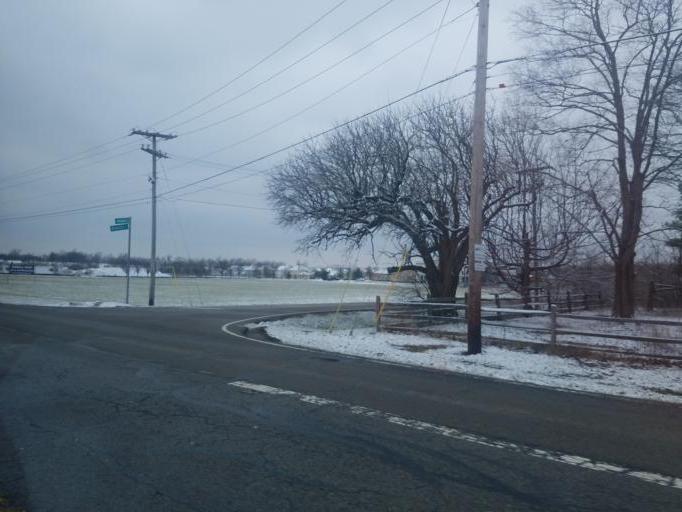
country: US
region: Ohio
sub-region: Franklin County
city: Reynoldsburg
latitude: 40.0019
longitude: -82.7911
